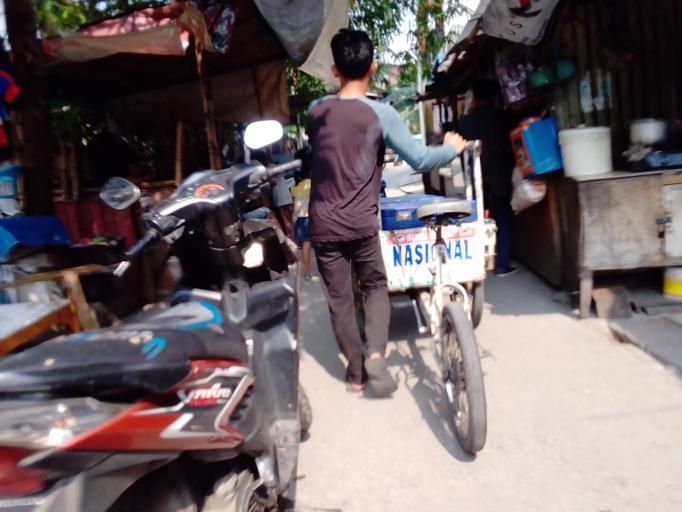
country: ID
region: Jakarta Raya
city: Jakarta
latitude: -6.2108
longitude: 106.7933
